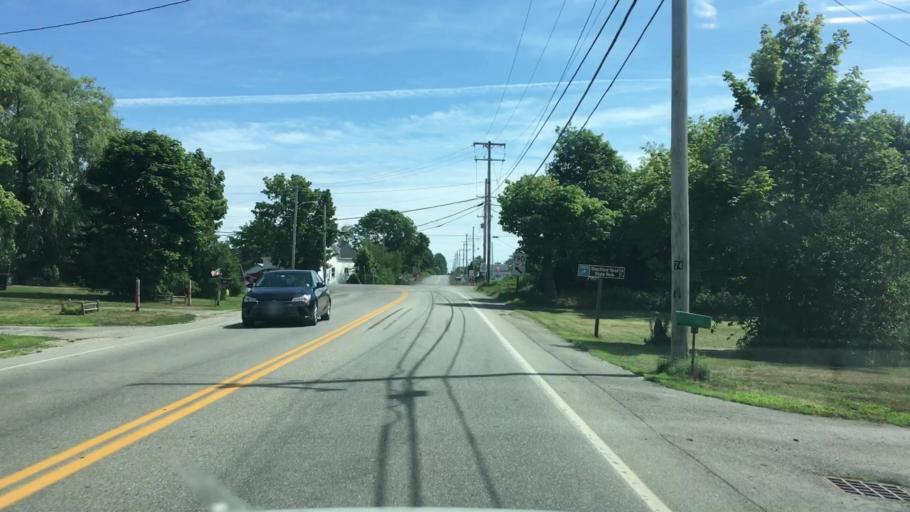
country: US
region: Maine
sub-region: Washington County
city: Eastport
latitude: 44.9075
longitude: -66.9978
